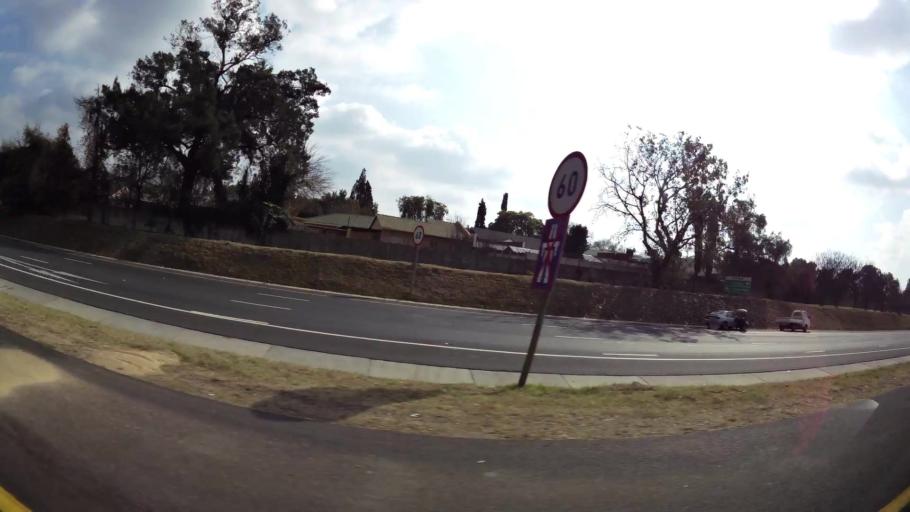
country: ZA
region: Gauteng
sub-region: Ekurhuleni Metropolitan Municipality
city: Benoni
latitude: -26.1760
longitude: 28.3318
